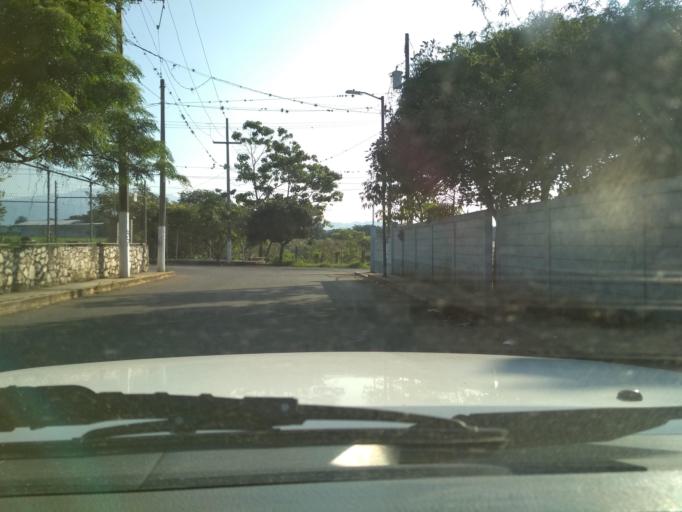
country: MX
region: Veracruz
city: Cordoba
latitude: 18.8698
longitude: -96.9291
